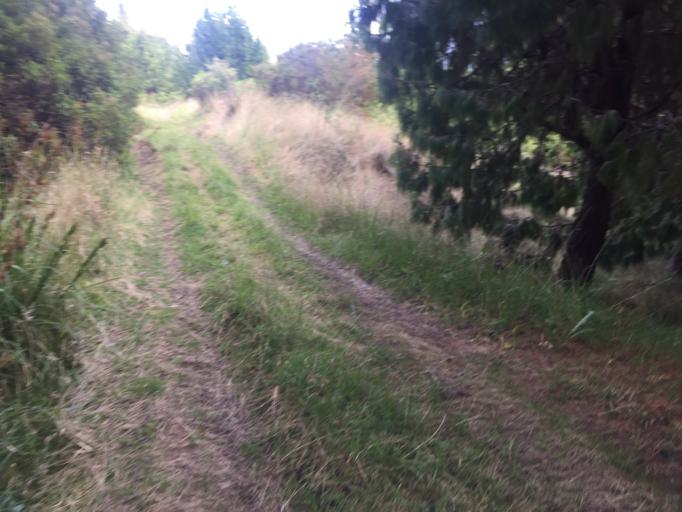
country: EC
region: Imbabura
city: Ibarra
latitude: 0.2252
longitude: -78.1262
